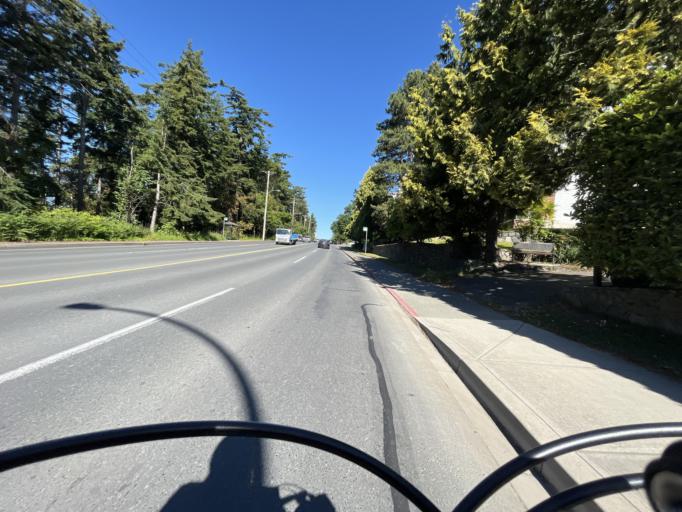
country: CA
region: British Columbia
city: Victoria
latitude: 48.4467
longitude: -123.3950
